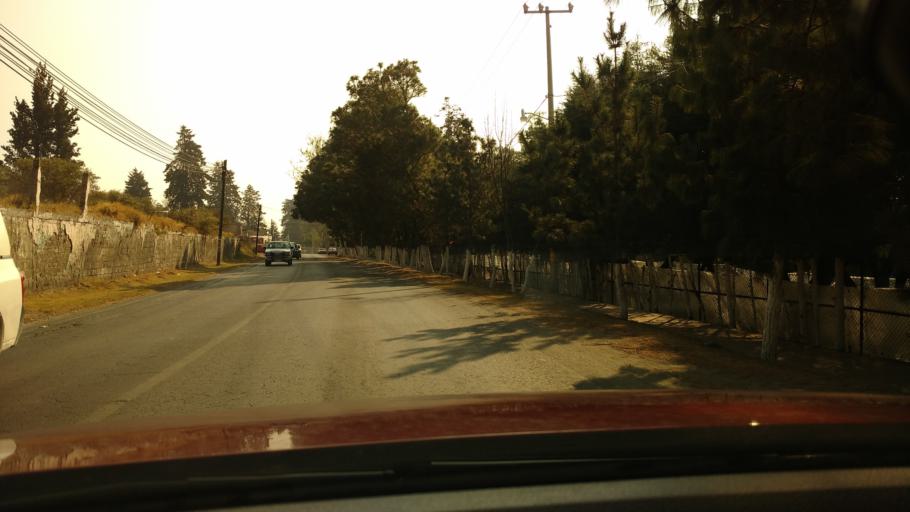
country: MX
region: Morelos
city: Chapultepec
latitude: 19.2031
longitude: -99.5578
